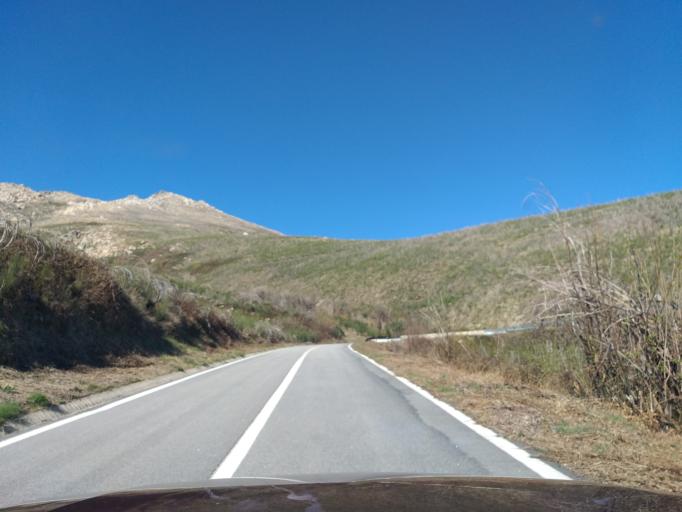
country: PT
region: Guarda
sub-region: Manteigas
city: Manteigas
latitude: 40.4713
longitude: -7.5196
